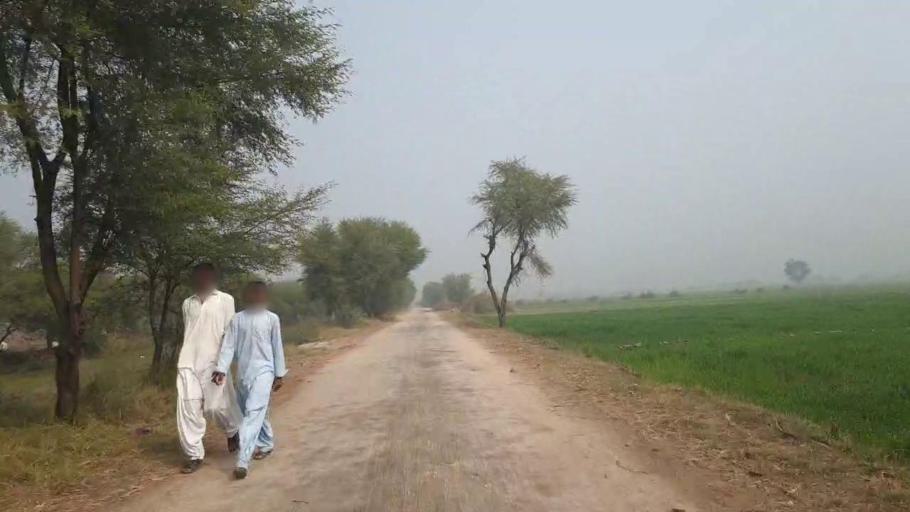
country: PK
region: Sindh
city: Bhit Shah
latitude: 25.8128
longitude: 68.5594
